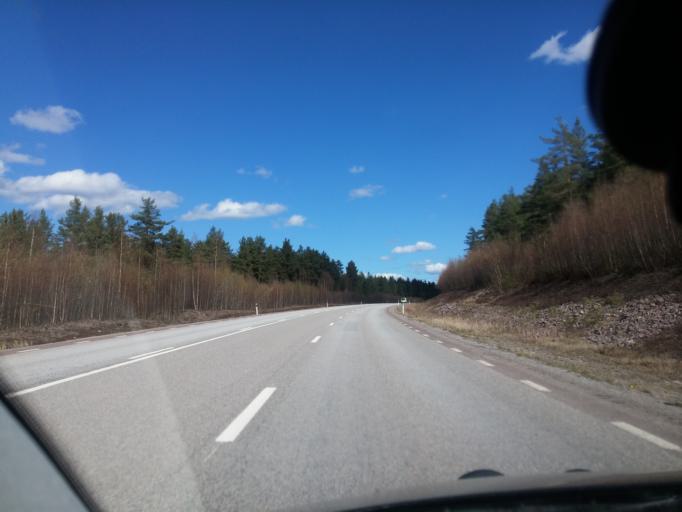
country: SE
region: Dalarna
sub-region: Faluns Kommun
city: Falun
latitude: 60.6407
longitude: 15.6260
